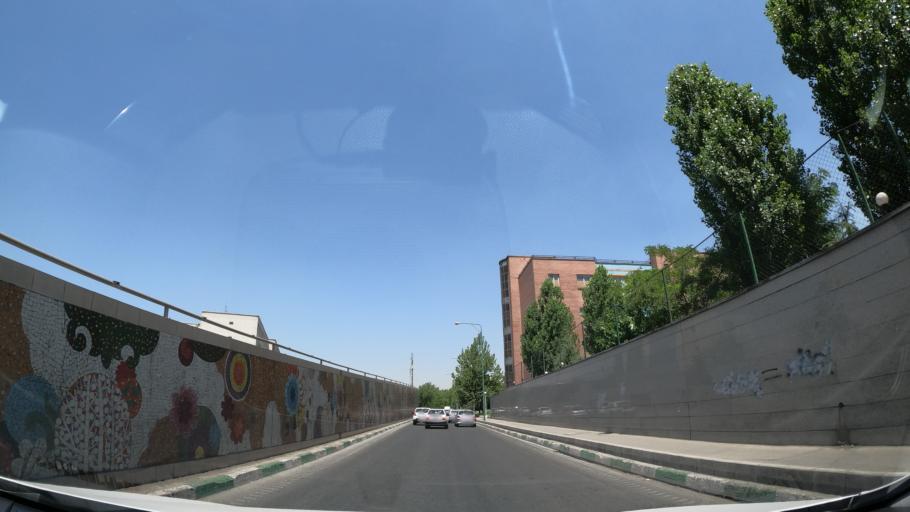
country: IR
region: Tehran
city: Tehran
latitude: 35.7283
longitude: 51.3708
